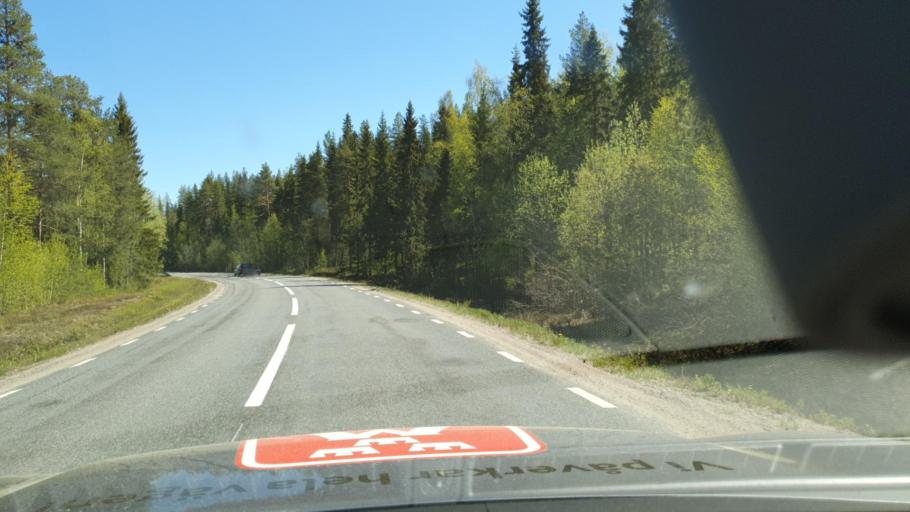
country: SE
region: Vaesternorrland
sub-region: OErnskoeldsviks Kommun
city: Bredbyn
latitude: 63.8061
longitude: 18.4836
